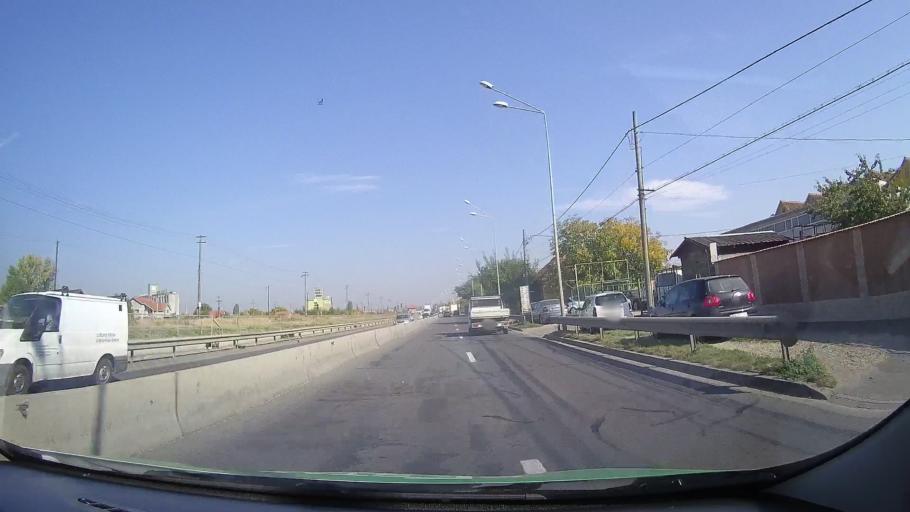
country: RO
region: Bihor
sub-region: Comuna Biharea
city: Oradea
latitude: 47.0592
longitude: 21.8936
